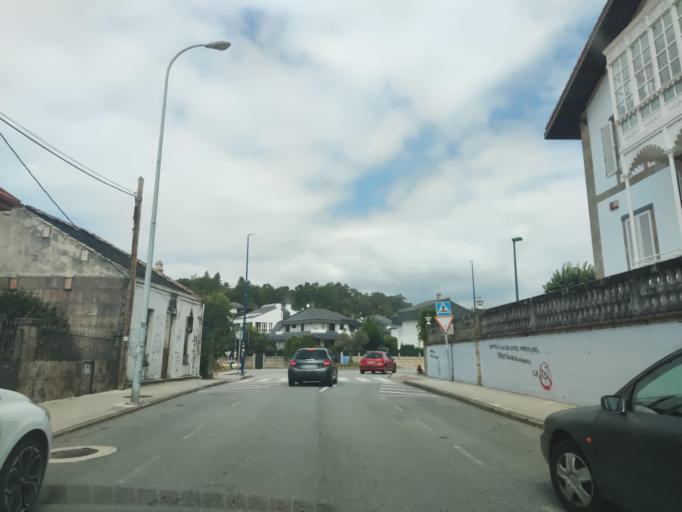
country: ES
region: Galicia
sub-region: Provincia de Pontevedra
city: Vigo
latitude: 42.2531
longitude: -8.6979
